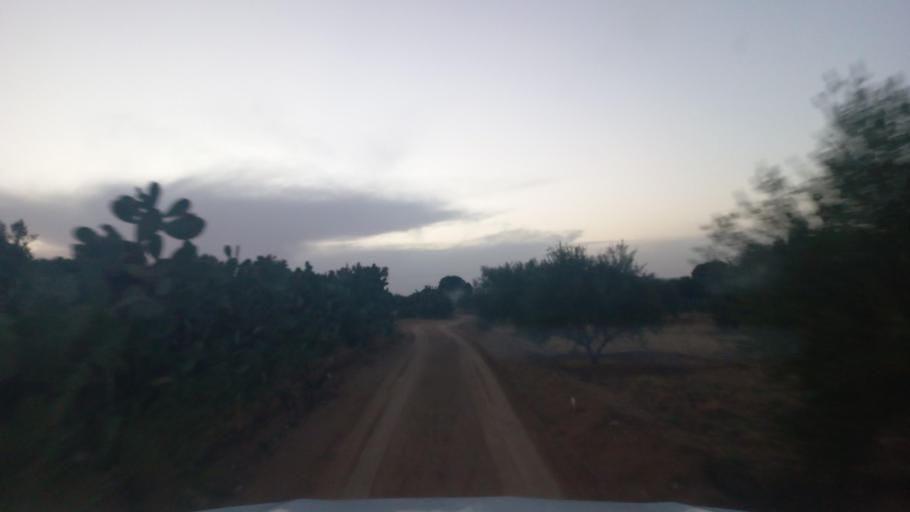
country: TN
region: Al Qasrayn
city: Kasserine
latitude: 35.2320
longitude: 9.0322
